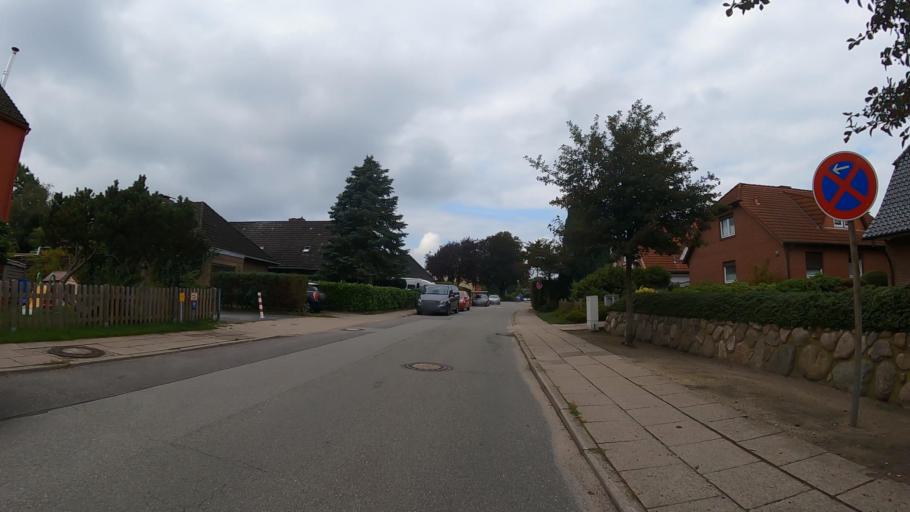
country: DE
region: Schleswig-Holstein
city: Tornesch
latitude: 53.6921
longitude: 9.7261
